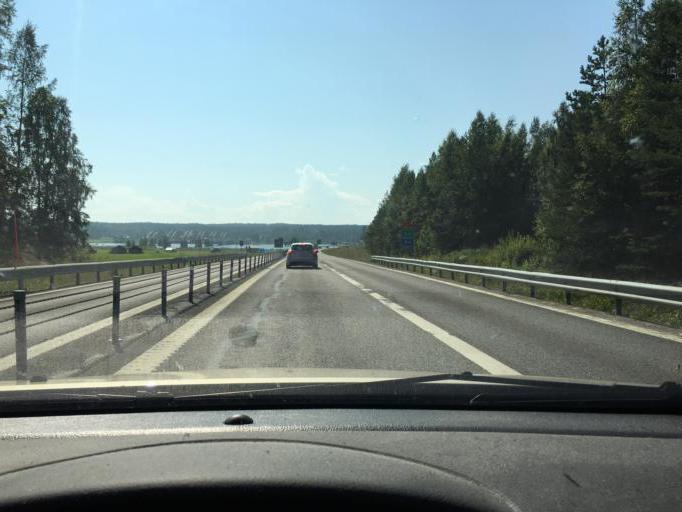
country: SE
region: Norrbotten
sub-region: Lulea Kommun
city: Gammelstad
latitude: 65.5963
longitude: 22.0414
